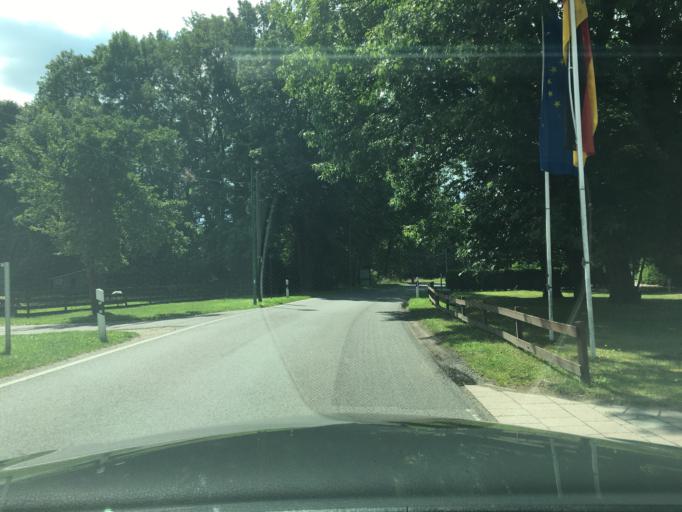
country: DE
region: Brandenburg
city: Burg
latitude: 51.8560
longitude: 14.1090
